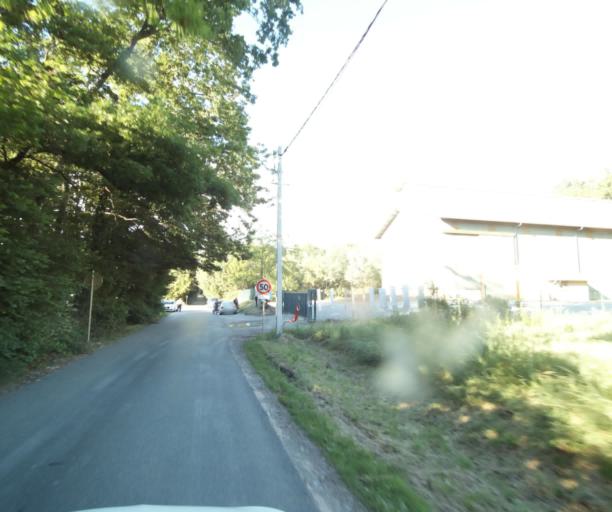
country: FR
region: Rhone-Alpes
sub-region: Departement de la Haute-Savoie
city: Loisin
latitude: 46.2719
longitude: 6.2923
